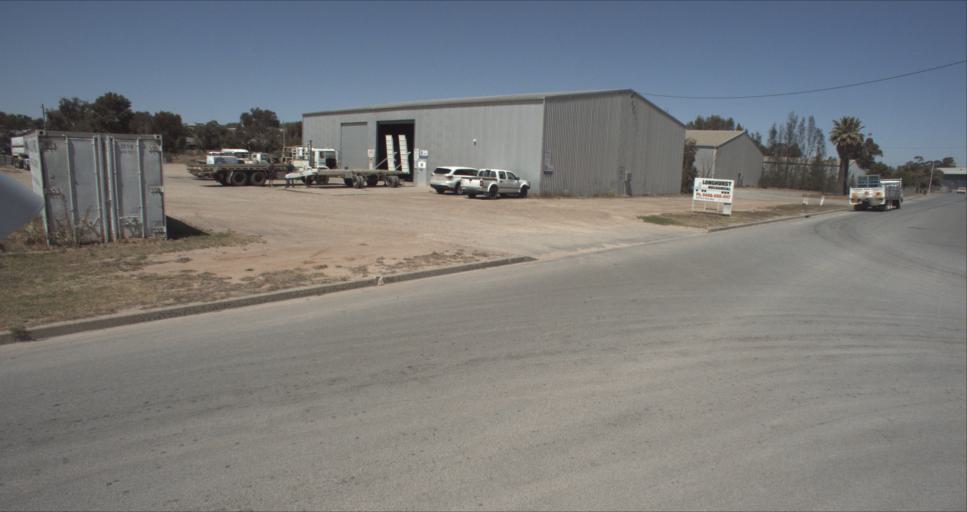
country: AU
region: New South Wales
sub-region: Leeton
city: Leeton
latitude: -34.5478
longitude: 146.3991
